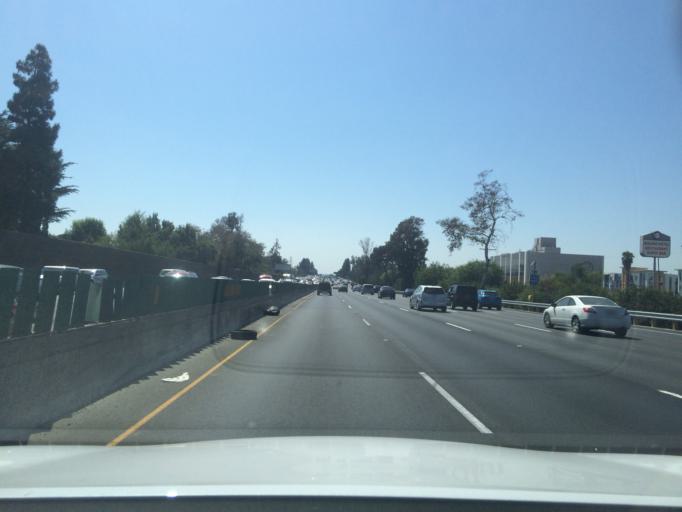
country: US
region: California
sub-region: Los Angeles County
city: North Hollywood
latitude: 34.1568
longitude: -118.4057
